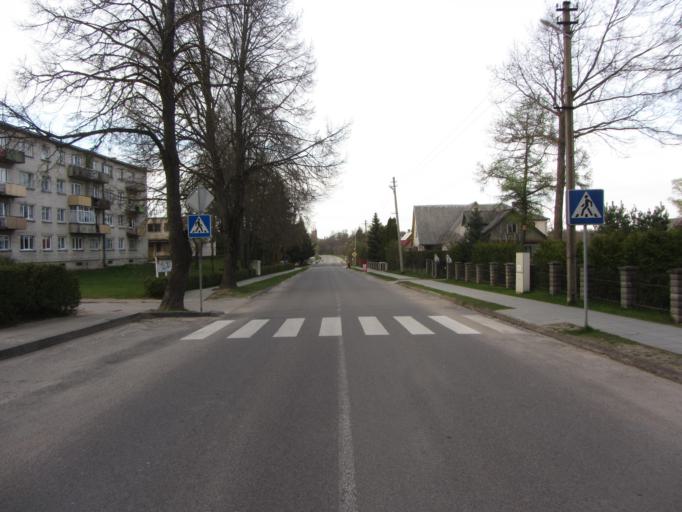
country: LT
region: Utenos apskritis
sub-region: Utena
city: Utena
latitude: 55.7377
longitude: 25.8336
